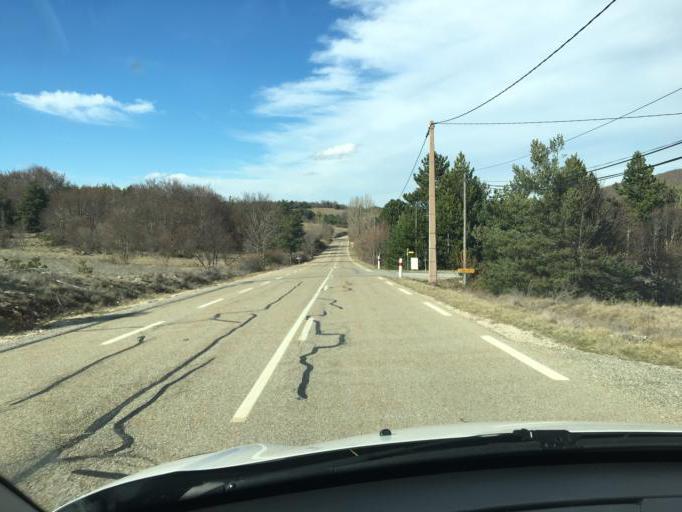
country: FR
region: Provence-Alpes-Cote d'Azur
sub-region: Departement du Vaucluse
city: Saint-Saturnin-les-Apt
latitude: 43.9804
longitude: 5.4721
